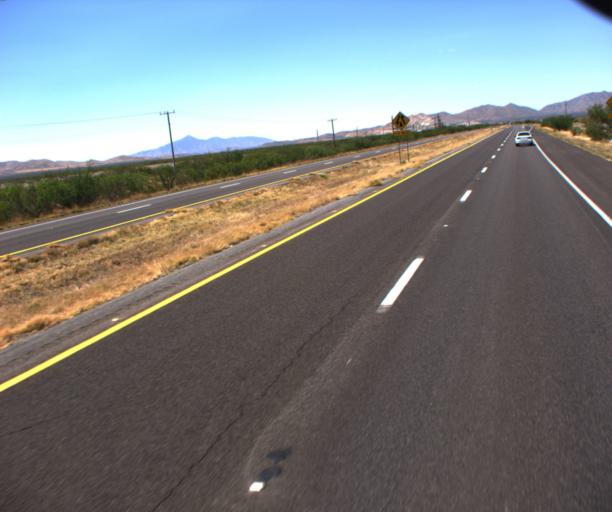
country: US
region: Arizona
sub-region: Cochise County
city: Pirtleville
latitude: 31.3641
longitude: -109.6949
